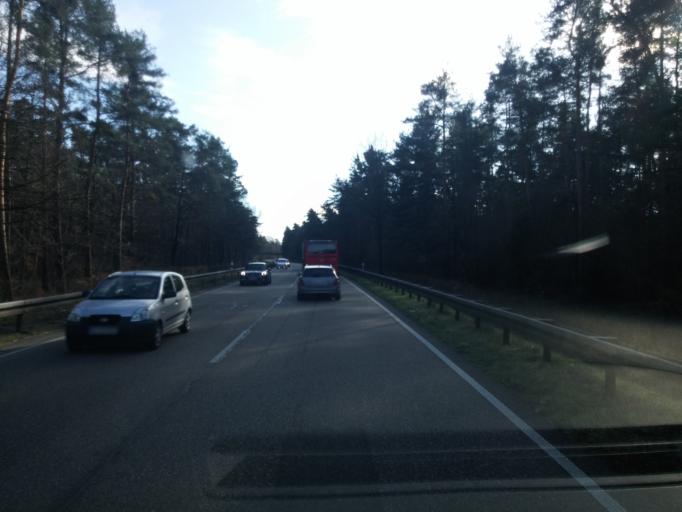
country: DE
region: Baden-Wuerttemberg
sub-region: Karlsruhe Region
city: Eggenstein-Leopoldshafen
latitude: 49.0624
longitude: 8.4533
